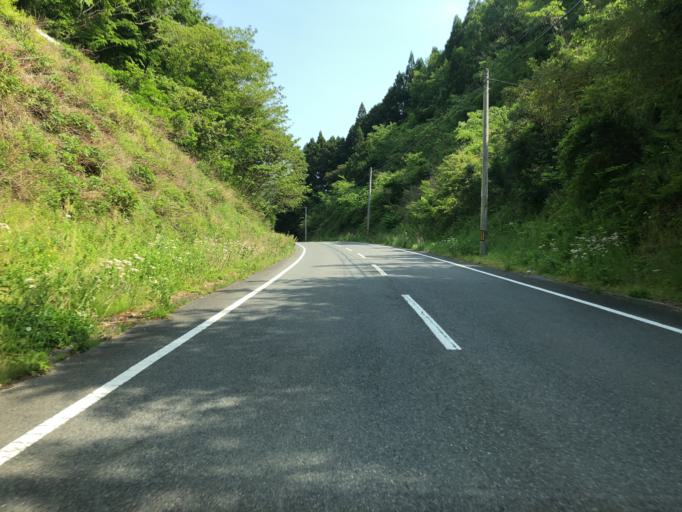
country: JP
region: Ibaraki
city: Kitaibaraki
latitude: 36.9513
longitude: 140.7062
